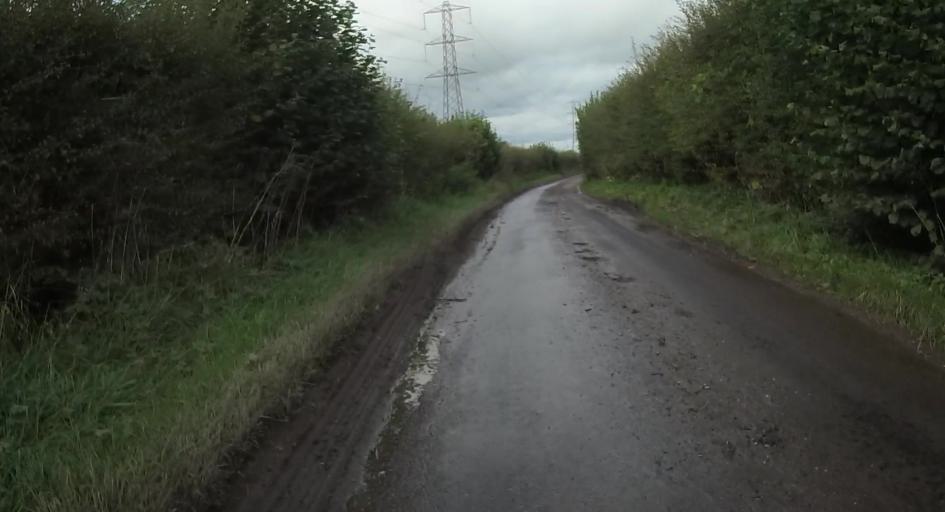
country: GB
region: England
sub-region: Hampshire
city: Alton
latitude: 51.1558
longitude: -0.9261
